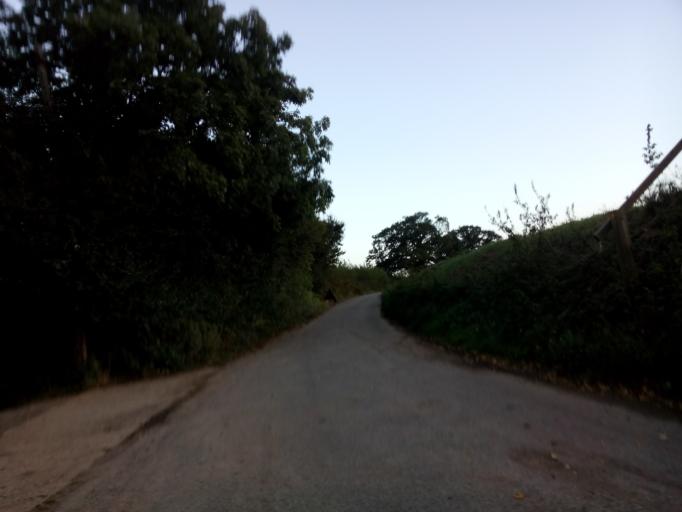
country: GB
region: England
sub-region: Suffolk
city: Bramford
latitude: 52.0555
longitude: 1.1057
